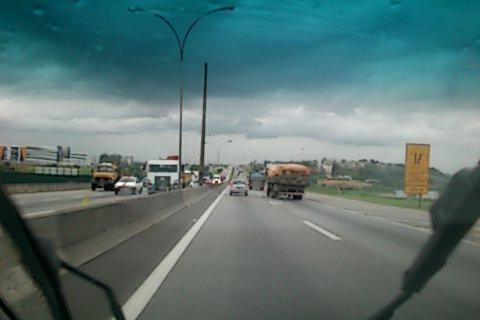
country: BR
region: Sao Paulo
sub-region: Jacarei
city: Jacarei
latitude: -23.2599
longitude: -45.9507
